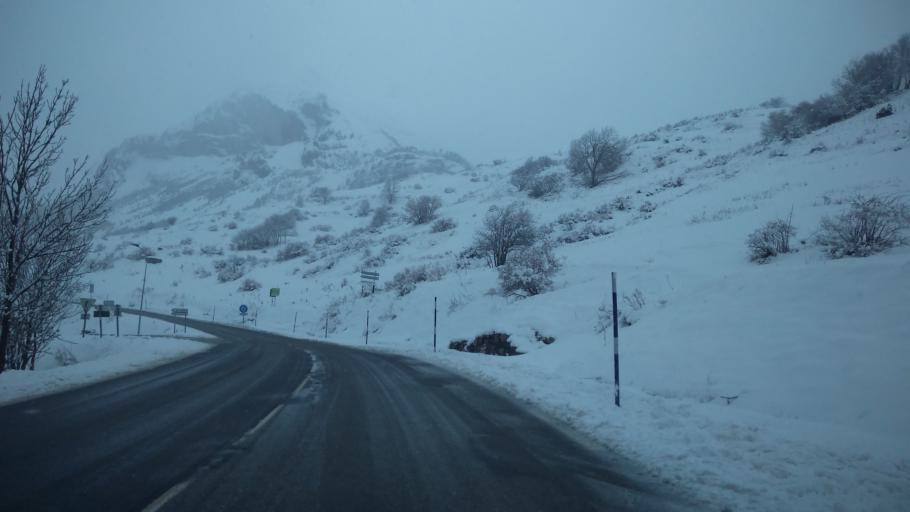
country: FR
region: Provence-Alpes-Cote d'Azur
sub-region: Departement des Hautes-Alpes
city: Le Monetier-les-Bains
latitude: 45.0136
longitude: 6.4676
